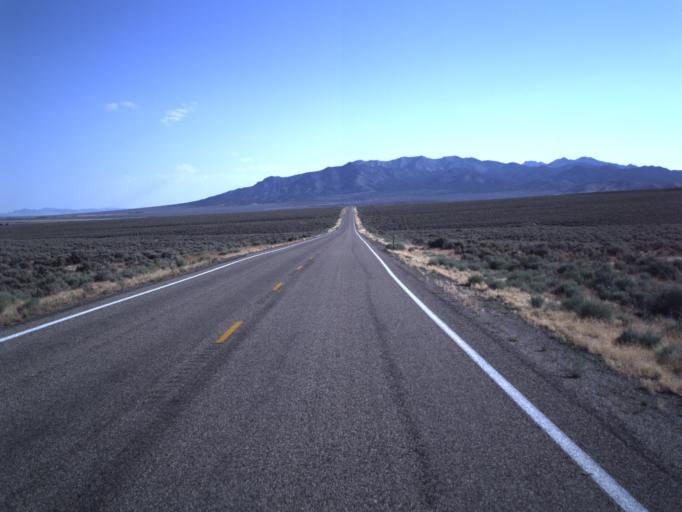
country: US
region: Utah
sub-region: Beaver County
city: Milford
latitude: 38.1523
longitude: -112.9592
